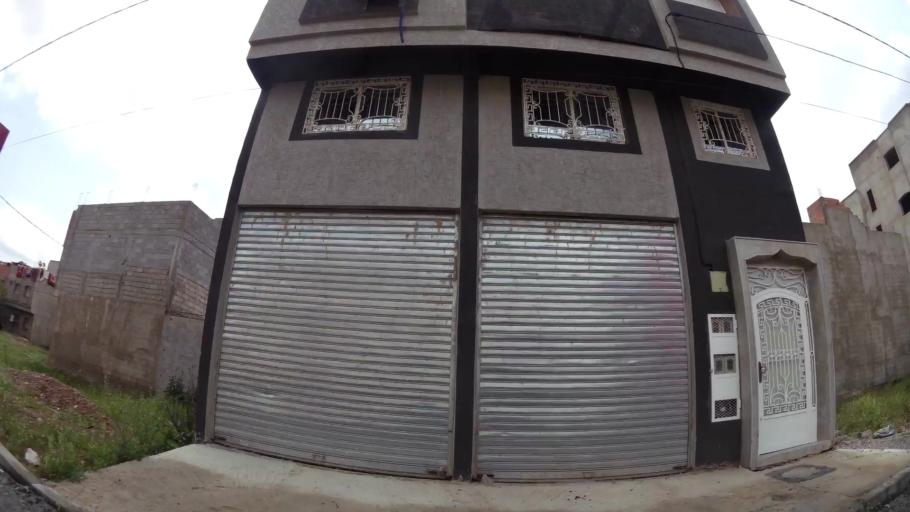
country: MA
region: Rabat-Sale-Zemmour-Zaer
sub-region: Khemisset
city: Tiflet
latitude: 33.8972
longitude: -6.3322
